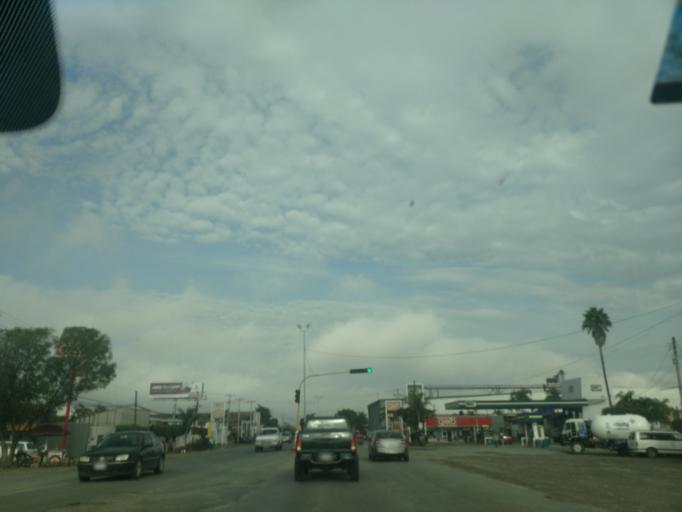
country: MX
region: Jalisco
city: Ameca
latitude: 20.5355
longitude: -104.0278
